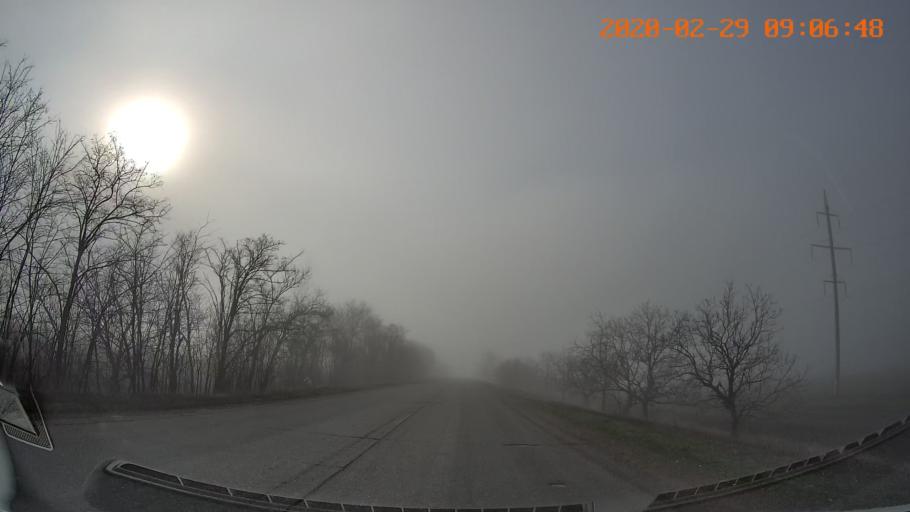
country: MD
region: Telenesti
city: Tiraspolul Nou
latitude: 46.8708
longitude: 29.7461
